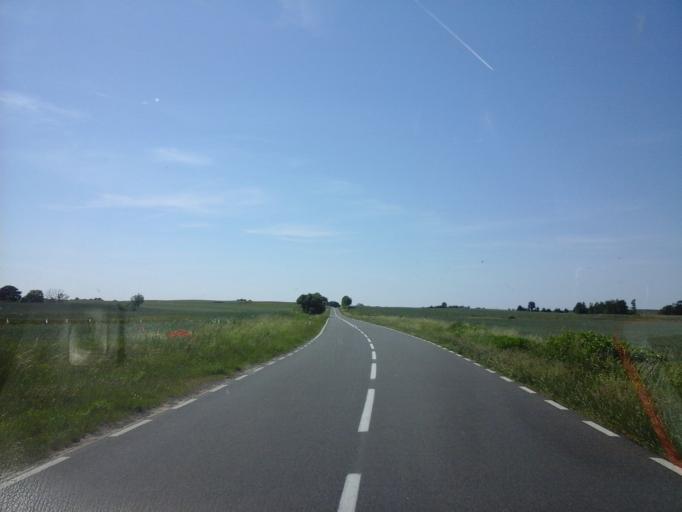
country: PL
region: West Pomeranian Voivodeship
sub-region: Powiat choszczenski
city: Bierzwnik
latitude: 53.1142
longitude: 15.6027
